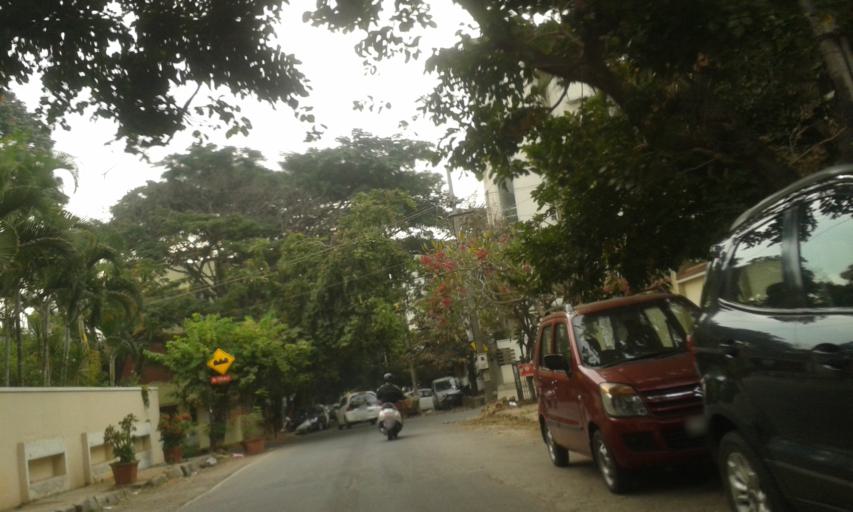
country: IN
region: Karnataka
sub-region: Bangalore Urban
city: Bangalore
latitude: 12.9358
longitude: 77.6257
